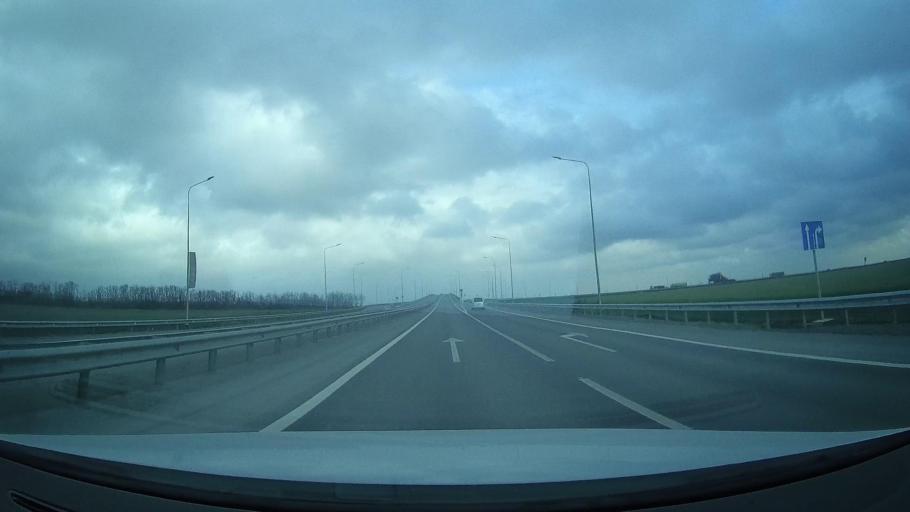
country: RU
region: Rostov
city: Grushevskaya
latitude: 47.4999
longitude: 39.9637
